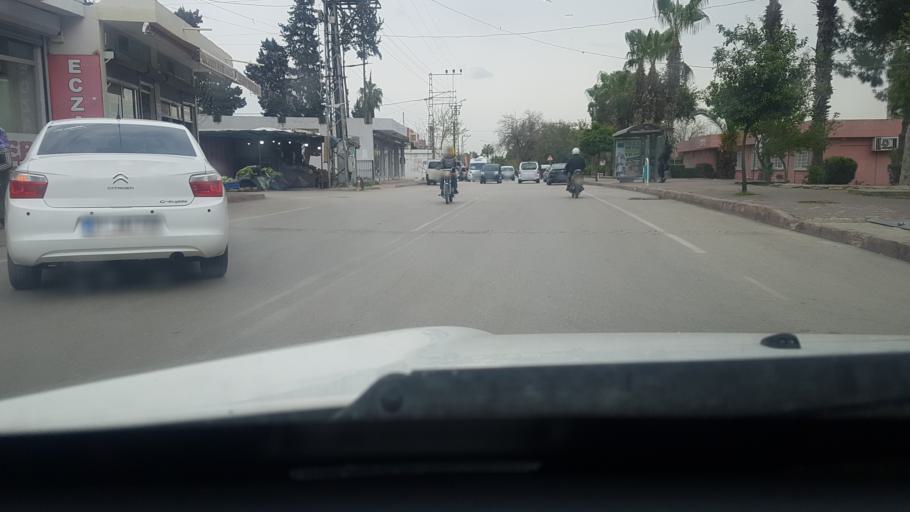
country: TR
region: Adana
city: Seyhan
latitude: 37.0133
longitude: 35.2794
